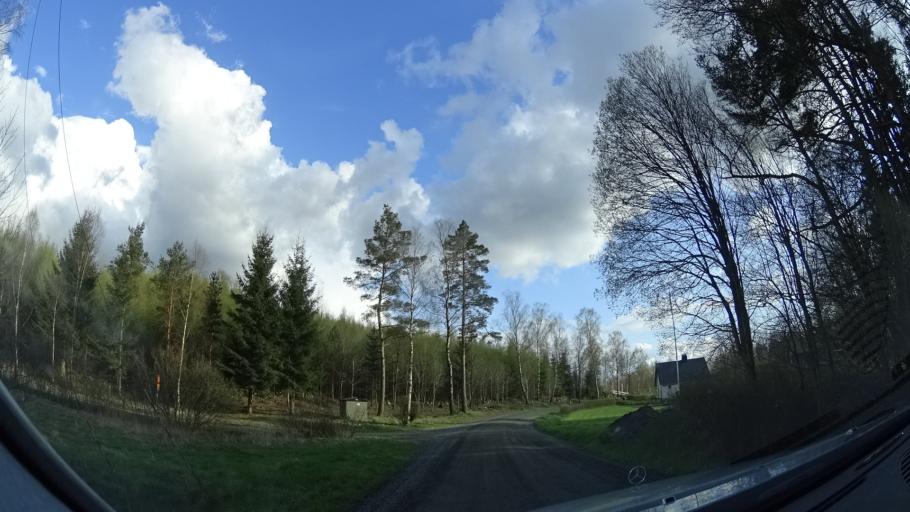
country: SE
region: Skane
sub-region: Perstorps Kommun
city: Perstorp
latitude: 56.1545
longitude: 13.3849
